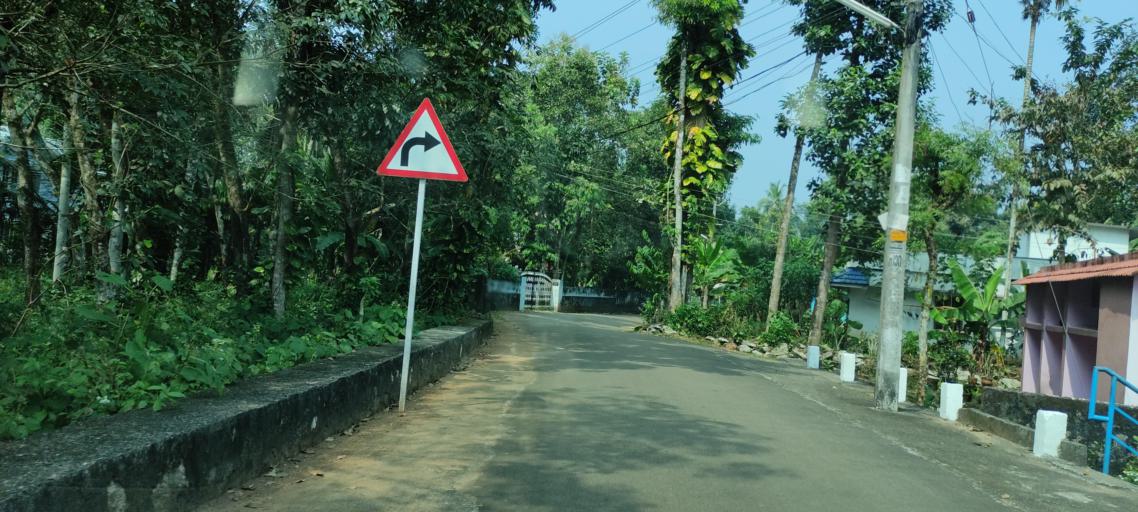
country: IN
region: Kerala
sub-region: Pattanamtitta
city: Adur
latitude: 9.2076
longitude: 76.6925
